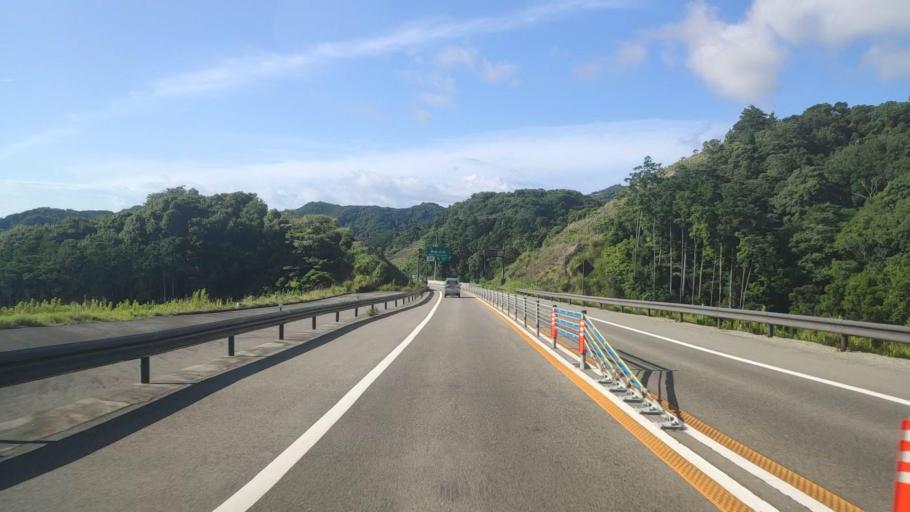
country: JP
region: Wakayama
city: Tanabe
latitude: 33.6445
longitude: 135.4099
